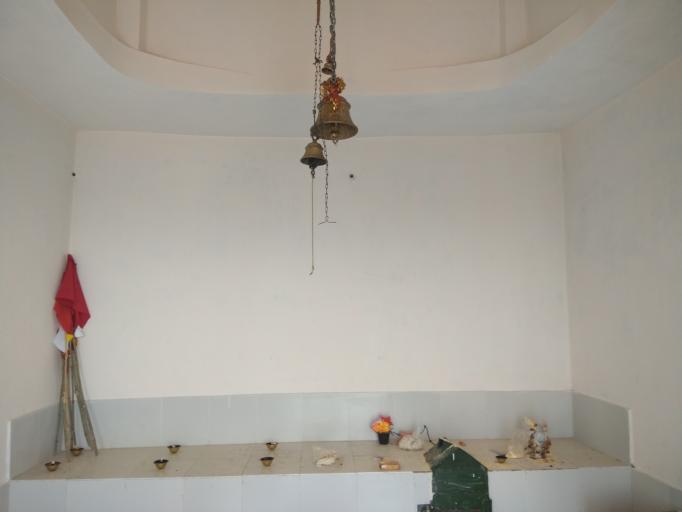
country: IN
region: Himachal Pradesh
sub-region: Kangra
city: Palampur
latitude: 32.0785
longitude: 76.6215
